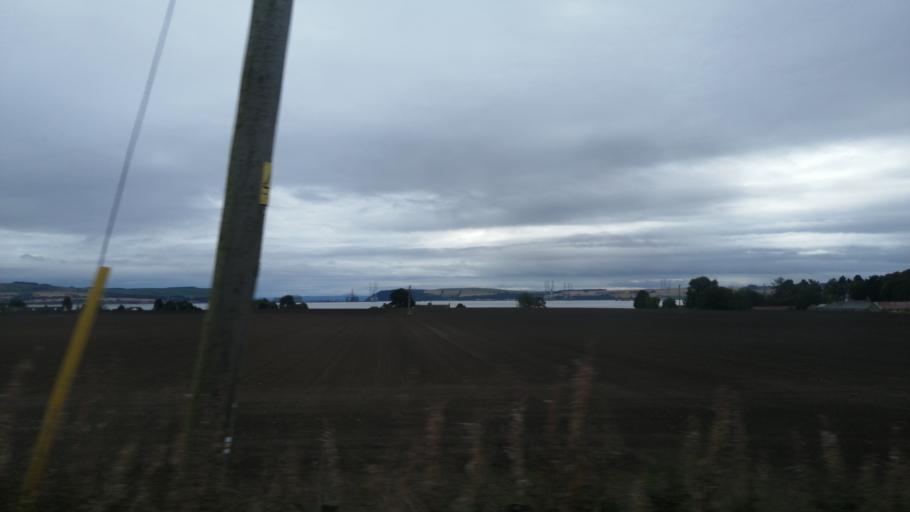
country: GB
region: Scotland
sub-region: Highland
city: Invergordon
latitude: 57.7230
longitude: -4.1125
